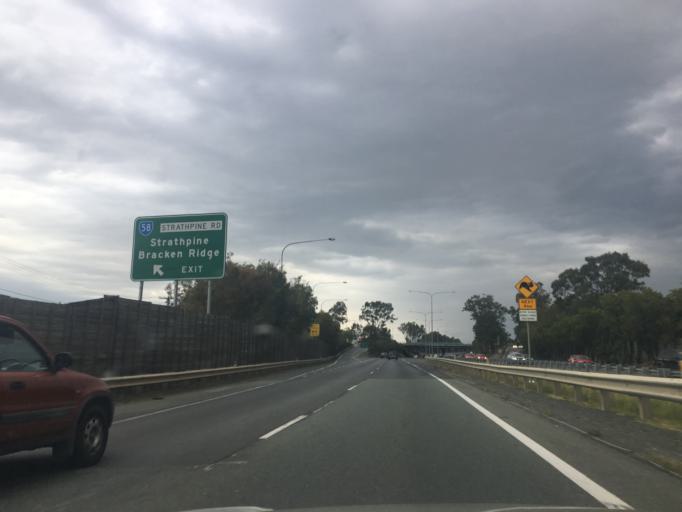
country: AU
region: Queensland
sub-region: Brisbane
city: Bald Hills
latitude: -27.3151
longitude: 153.0120
